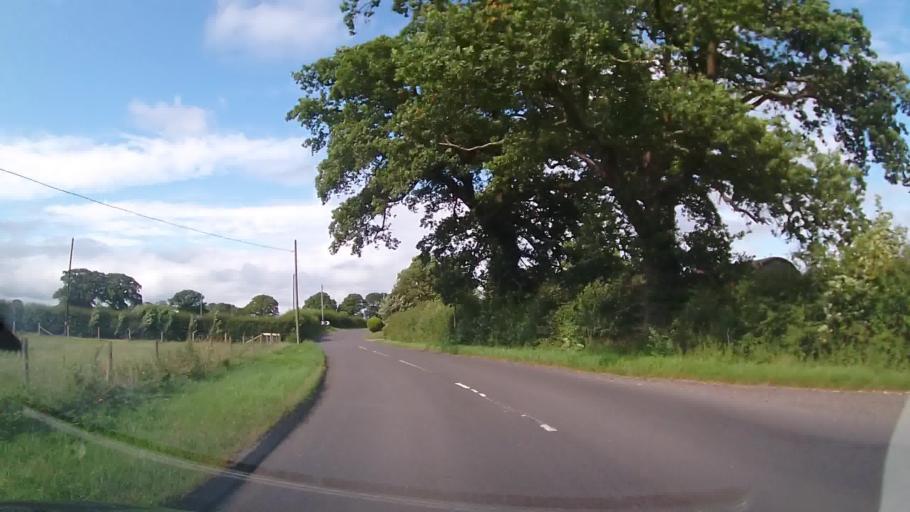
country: GB
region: England
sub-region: Shropshire
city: Petton
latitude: 52.8135
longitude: -2.8214
